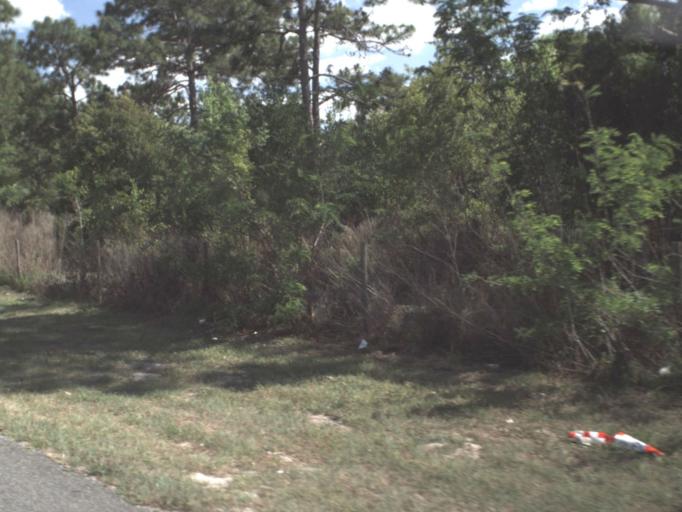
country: US
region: Florida
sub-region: Lake County
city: Mount Plymouth
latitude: 28.8160
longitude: -81.4719
